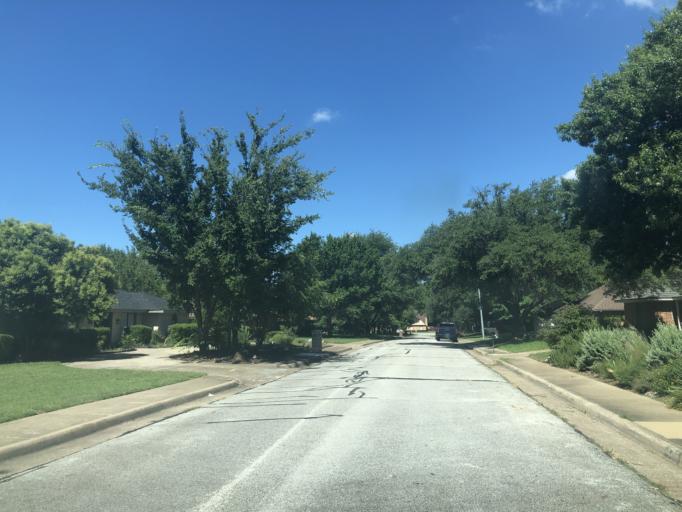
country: US
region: Texas
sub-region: Dallas County
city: Duncanville
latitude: 32.6427
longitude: -96.9358
